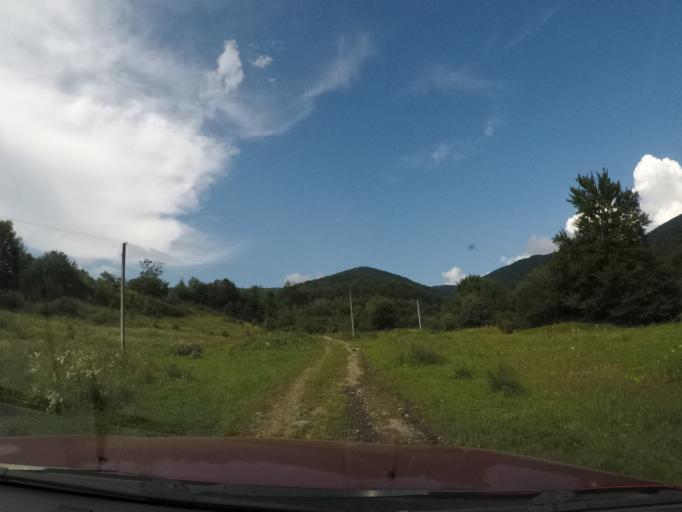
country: PL
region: Subcarpathian Voivodeship
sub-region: Powiat bieszczadzki
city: Lutowiska
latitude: 49.0303
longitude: 22.6483
